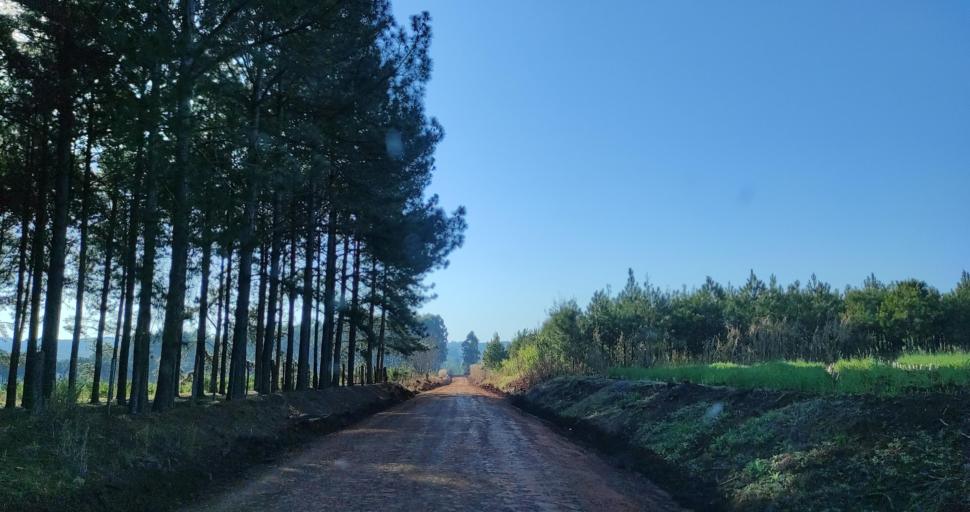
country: AR
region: Misiones
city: Capiovi
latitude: -26.8801
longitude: -55.0408
